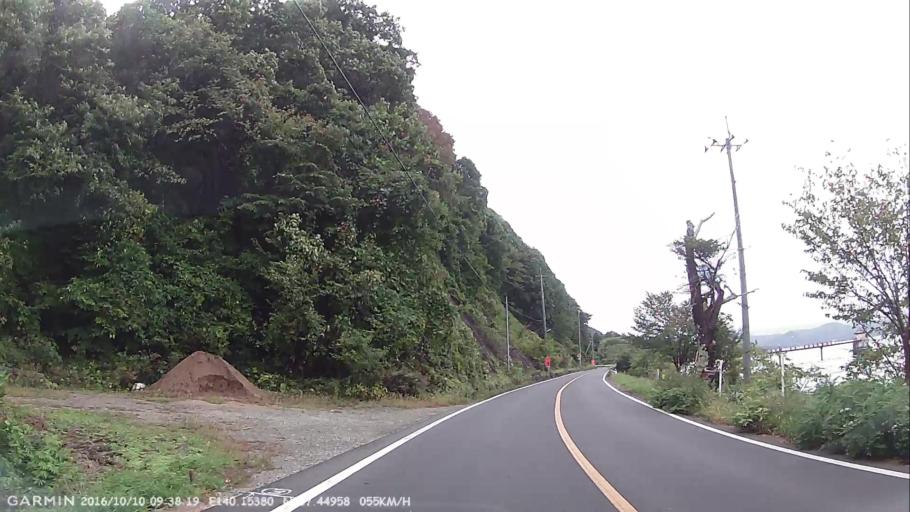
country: JP
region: Fukushima
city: Inawashiro
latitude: 37.4496
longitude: 140.1538
